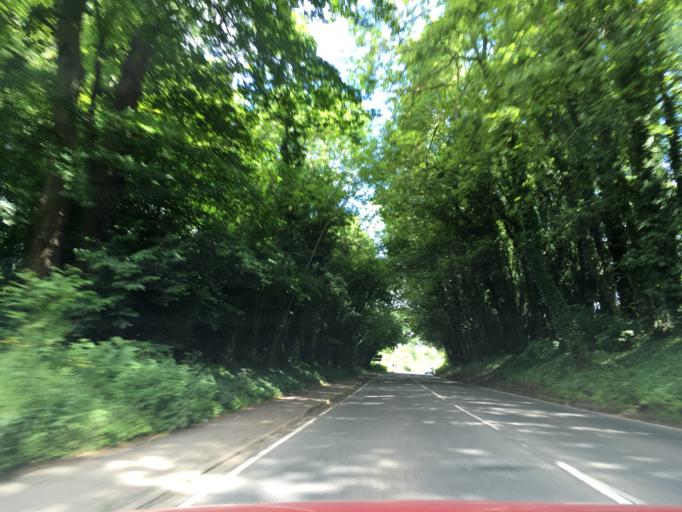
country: GB
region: England
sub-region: Oxfordshire
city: Bloxham
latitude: 52.0360
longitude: -1.3642
